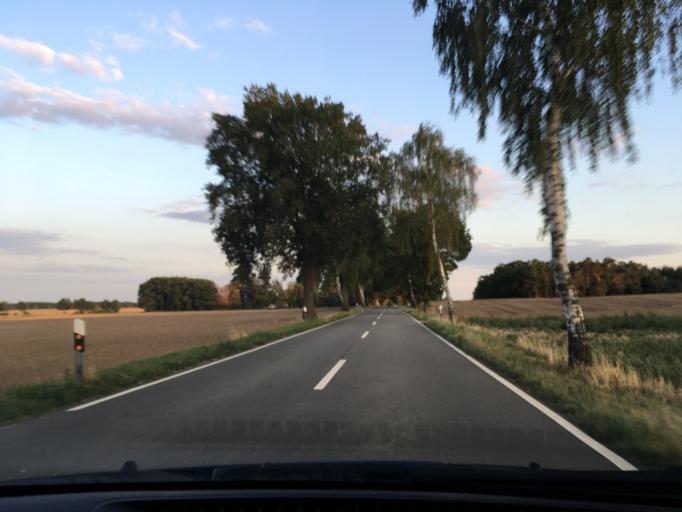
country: DE
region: Lower Saxony
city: Tosterglope
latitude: 53.2188
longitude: 10.8127
